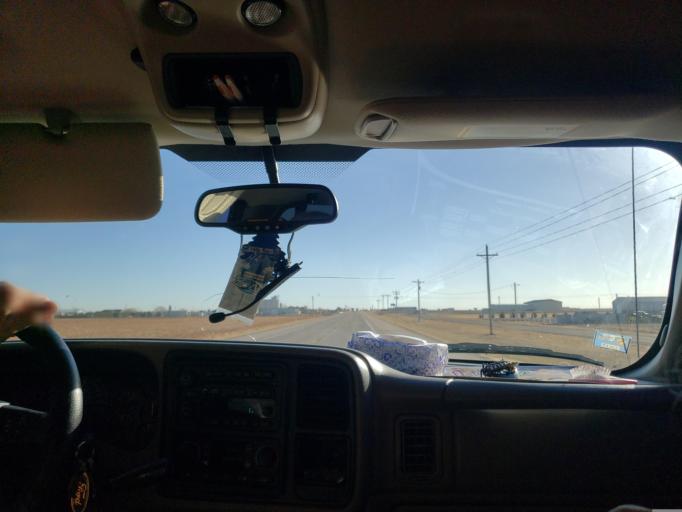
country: US
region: Kansas
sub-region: Haskell County
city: Sublette
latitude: 37.4916
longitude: -100.8701
